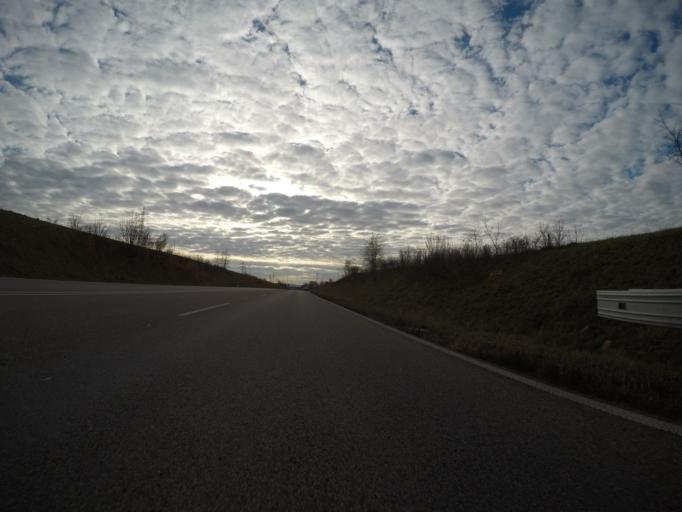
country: DE
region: Thuringia
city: Gossnitz
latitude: 50.8941
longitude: 12.4435
